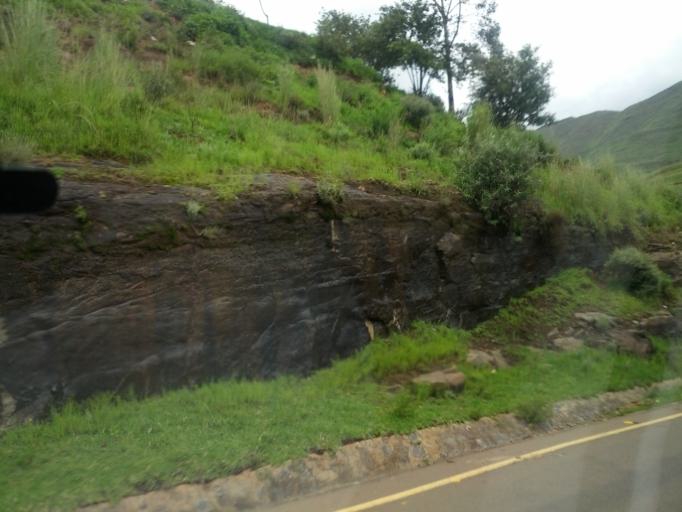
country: LS
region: Butha-Buthe
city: Butha-Buthe
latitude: -29.0373
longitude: 28.2799
